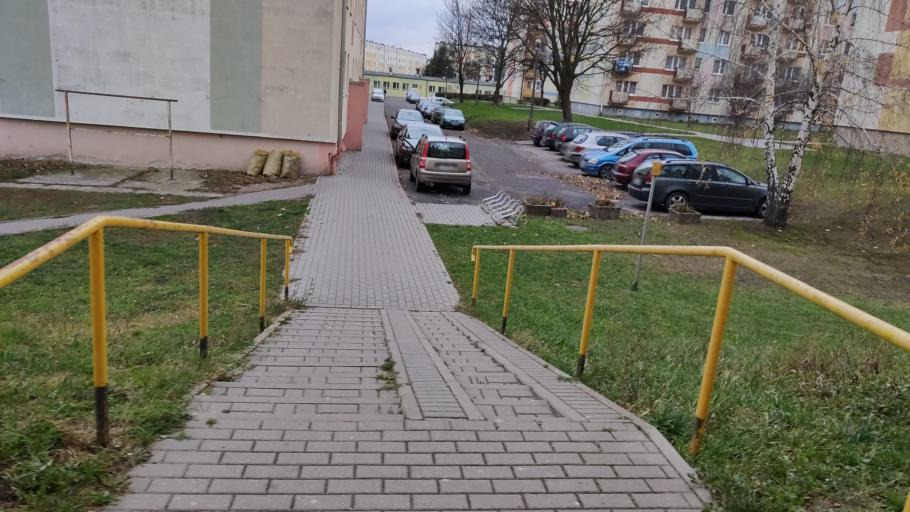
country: PL
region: Kujawsko-Pomorskie
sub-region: Powiat zninski
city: Barcin
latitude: 52.8529
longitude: 17.9437
